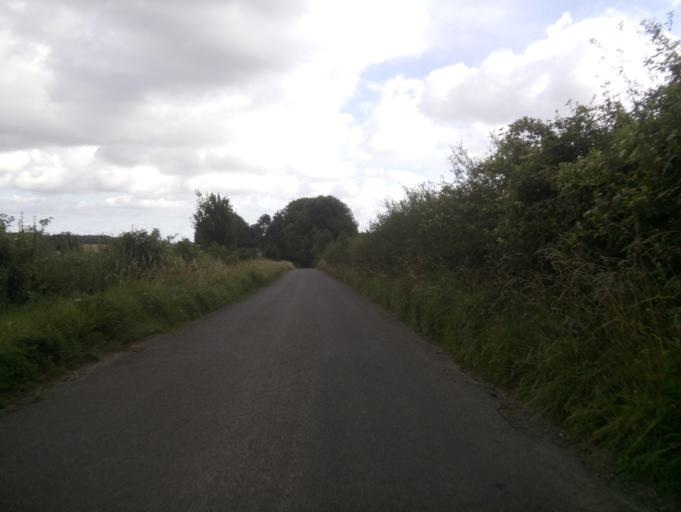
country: GB
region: England
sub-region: Gloucestershire
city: Chalford
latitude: 51.7671
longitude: -2.0906
